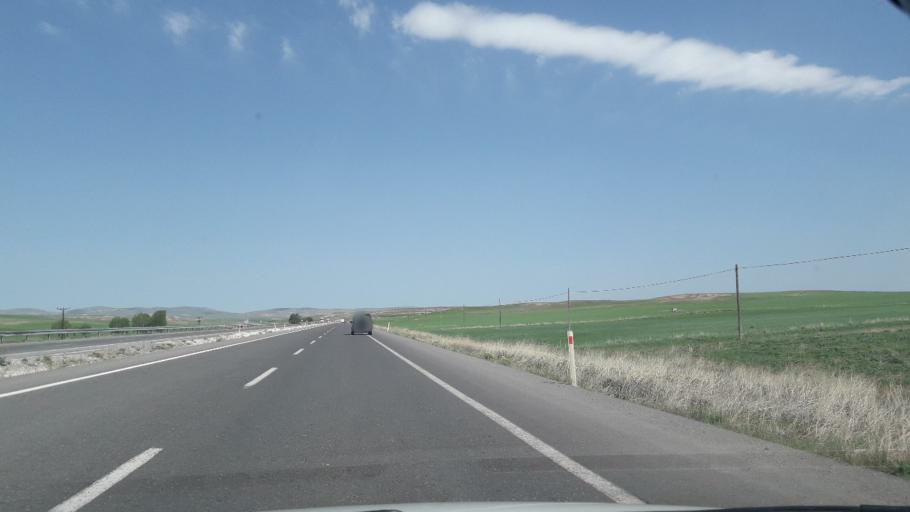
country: TR
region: Sivas
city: Deliktas
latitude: 39.2163
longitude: 37.1965
